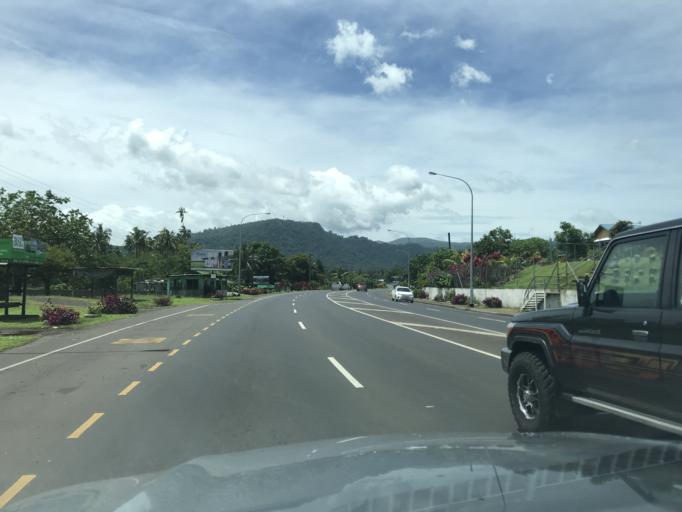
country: WS
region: Tuamasaga
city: Vaiusu
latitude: -13.8280
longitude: -171.7926
